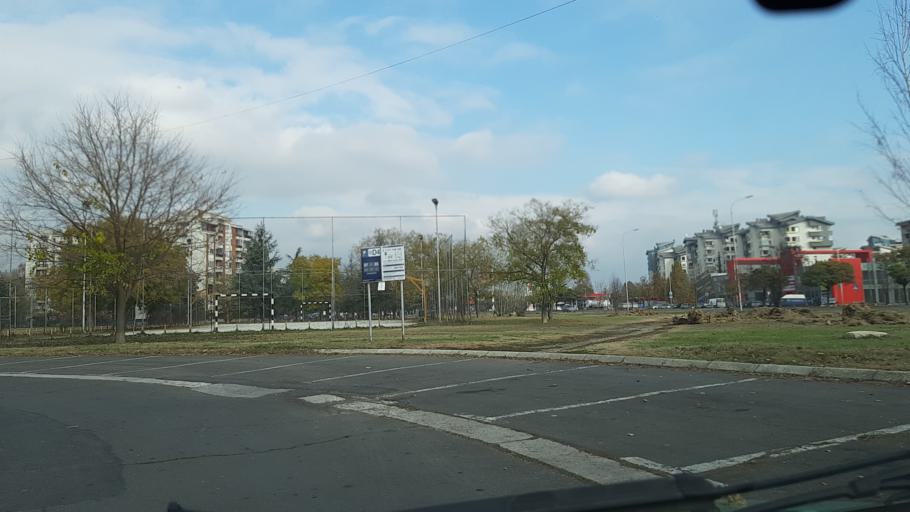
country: MK
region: Kisela Voda
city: Usje
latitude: 41.9855
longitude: 21.4722
